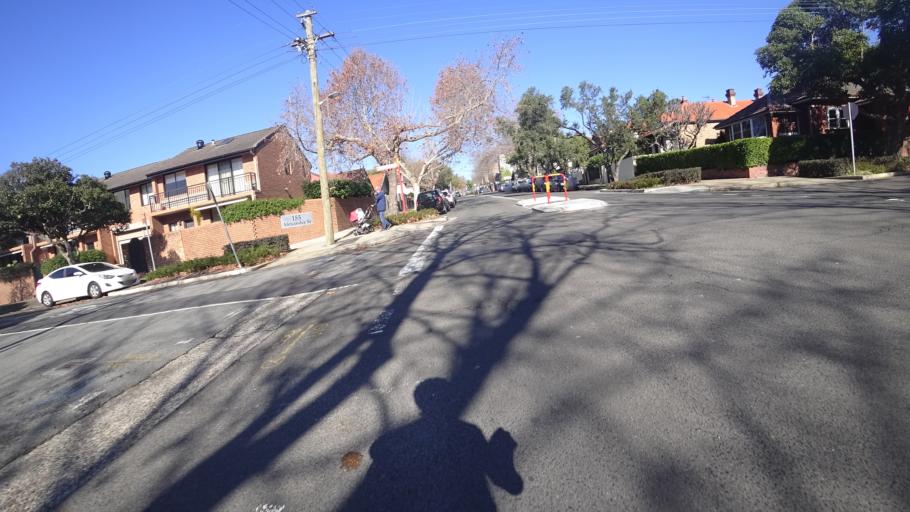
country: AU
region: New South Wales
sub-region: North Sydney
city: Crows Nest
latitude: -33.8232
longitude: 151.2030
